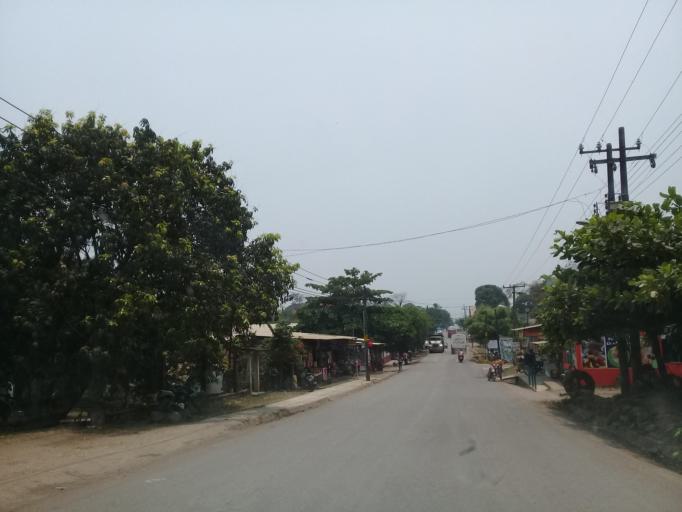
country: MX
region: Veracruz
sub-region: Tezonapa
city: Laguna Chica (Pueblo Nuevo)
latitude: 18.5446
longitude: -96.7339
